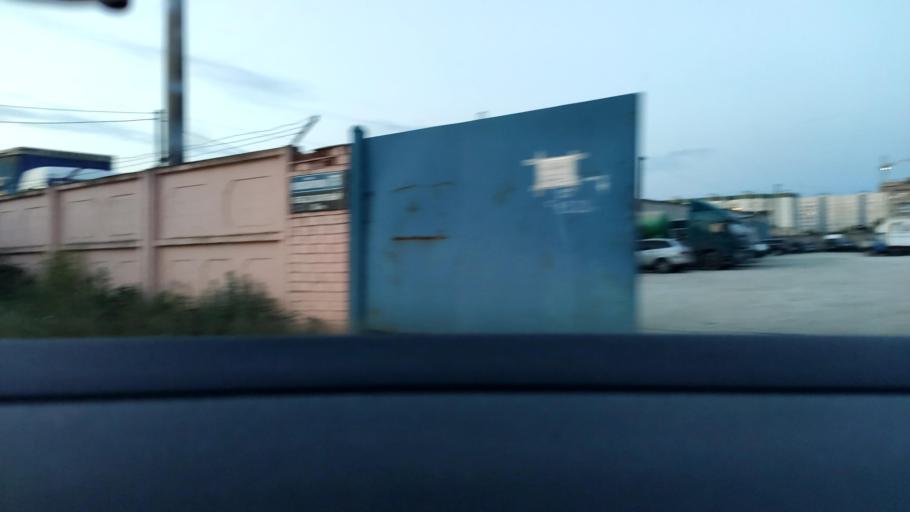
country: RU
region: Voronezj
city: Maslovka
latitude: 51.5896
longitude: 39.2373
